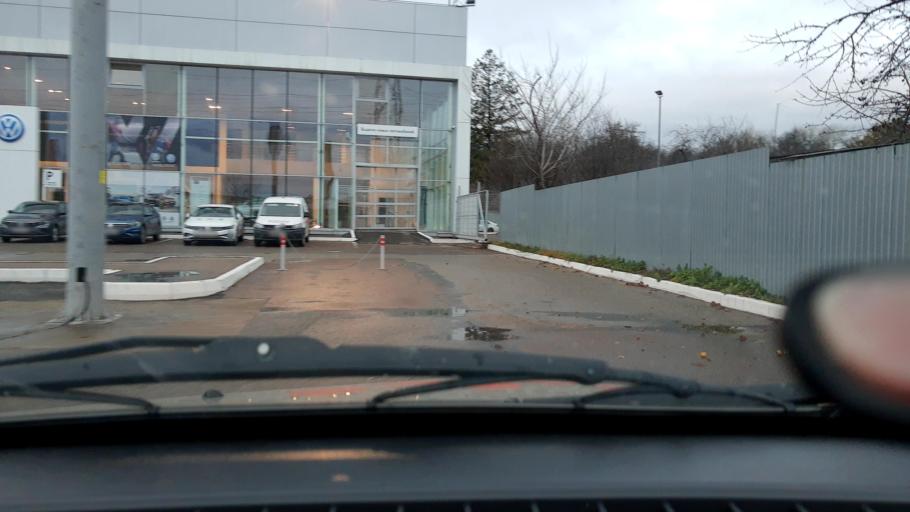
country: RU
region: Bashkortostan
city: Ufa
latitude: 54.8006
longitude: 56.0559
